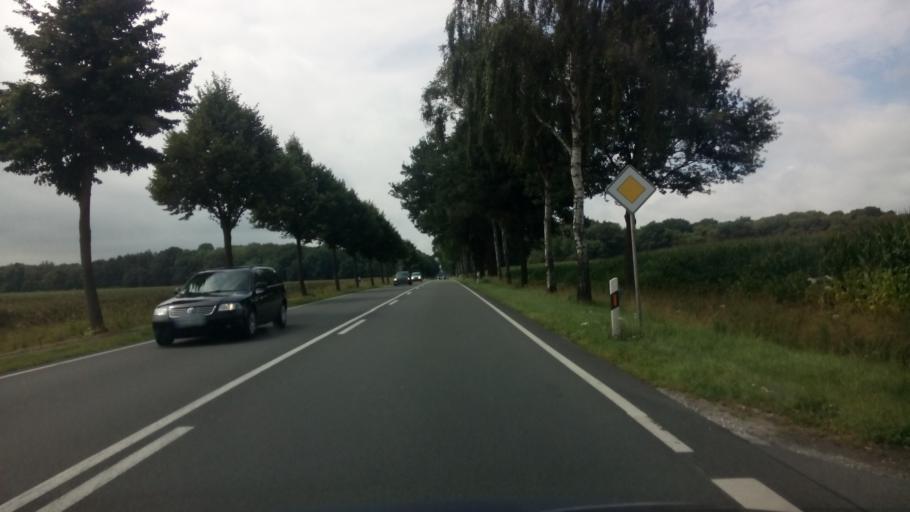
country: DE
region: Lower Saxony
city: Bassum
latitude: 52.8243
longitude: 8.6852
